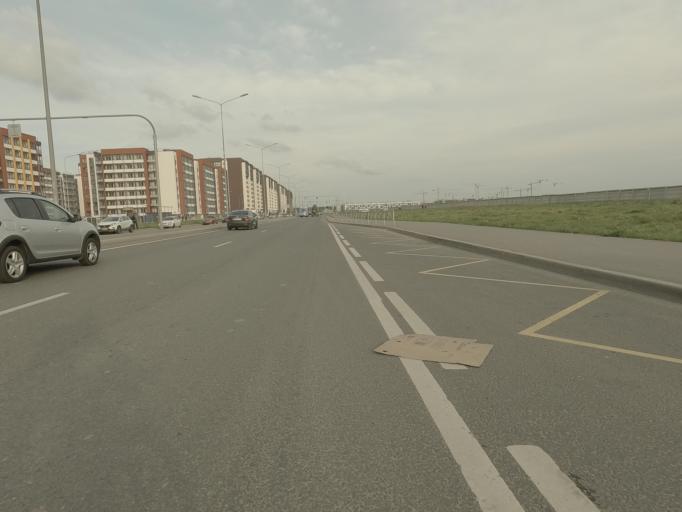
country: RU
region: St.-Petersburg
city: Sosnovaya Polyana
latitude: 59.8390
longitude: 30.0984
